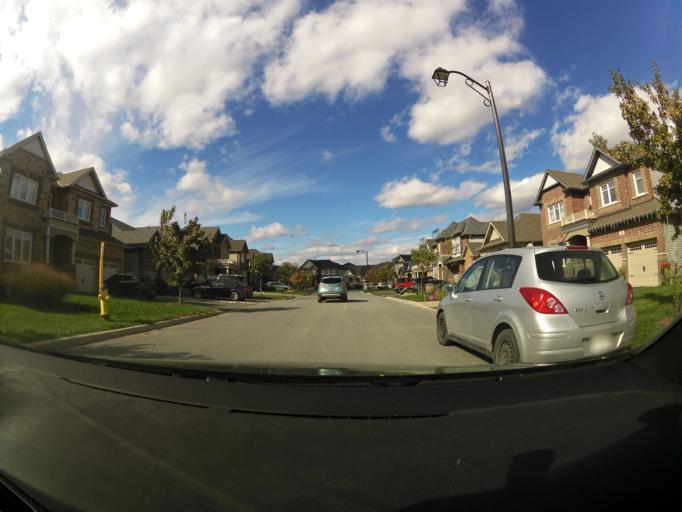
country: CA
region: Ontario
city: Bells Corners
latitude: 45.2753
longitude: -75.8870
